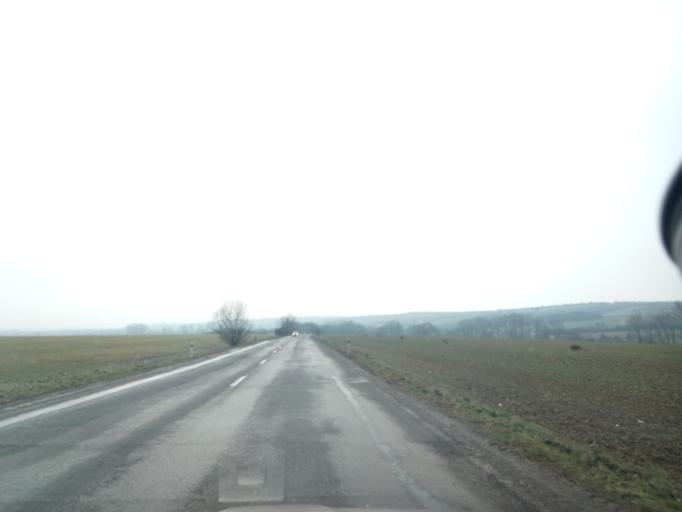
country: SK
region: Kosicky
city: Secovce
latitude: 48.6325
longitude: 21.5837
